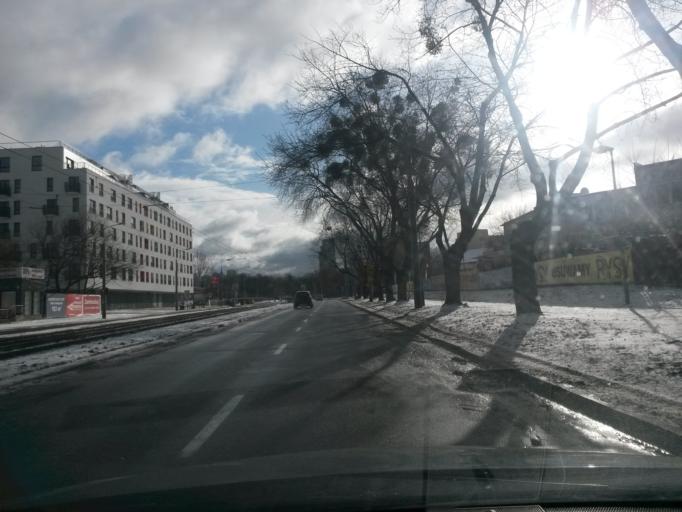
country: PL
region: Masovian Voivodeship
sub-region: Warszawa
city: Wola
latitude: 52.2451
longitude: 20.9646
